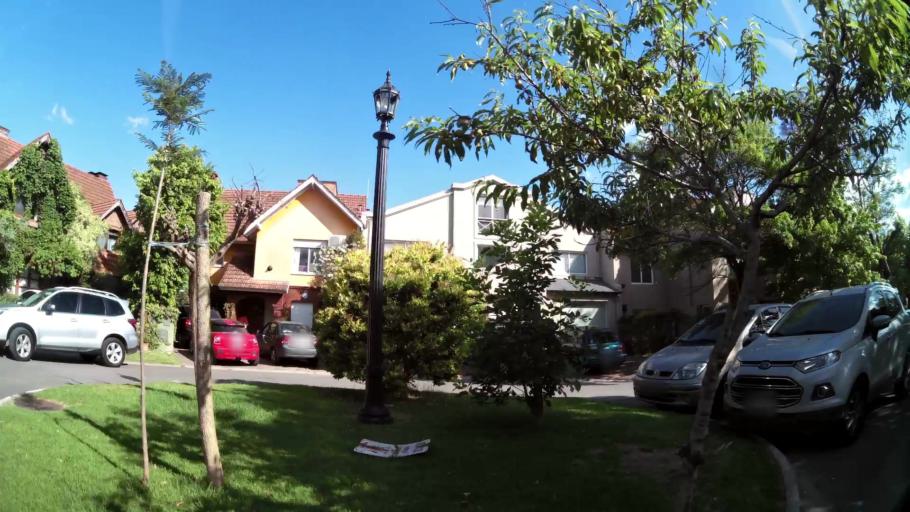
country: AR
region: Buenos Aires
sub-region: Partido de Tigre
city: Tigre
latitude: -34.4727
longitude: -58.5619
